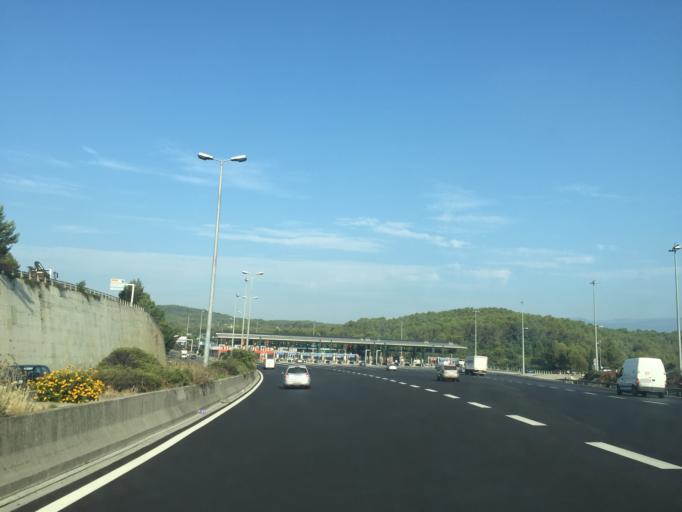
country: FR
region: Provence-Alpes-Cote d'Azur
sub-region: Departement des Alpes-Maritimes
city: Vallauris
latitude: 43.6042
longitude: 7.0693
